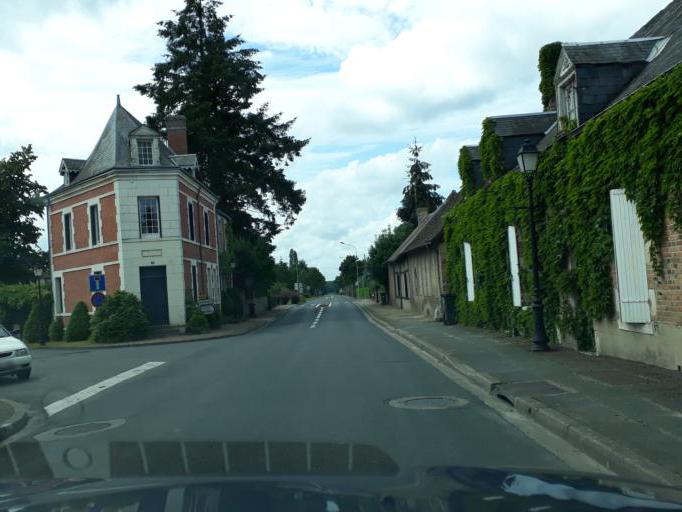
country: FR
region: Centre
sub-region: Departement du Loir-et-Cher
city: Chaumont-sur-Tharonne
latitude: 47.6086
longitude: 1.9035
